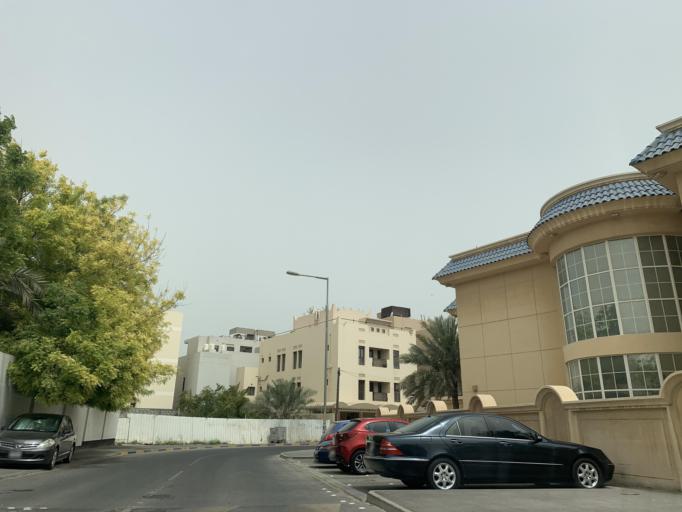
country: BH
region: Manama
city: Jidd Hafs
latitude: 26.2269
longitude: 50.5353
